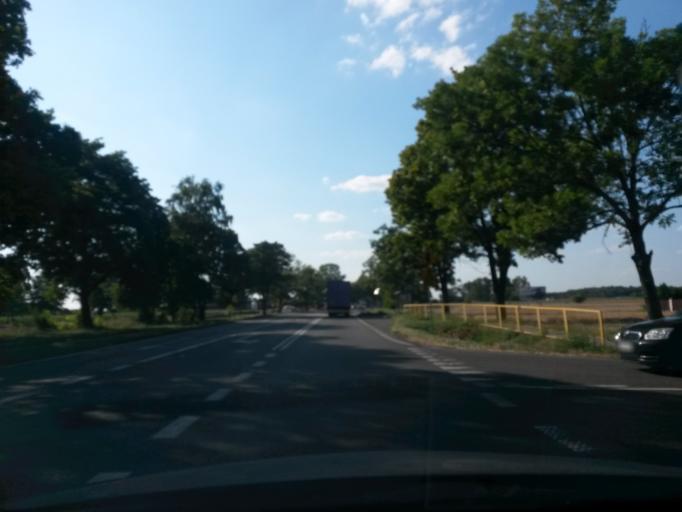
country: PL
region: Masovian Voivodeship
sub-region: Powiat sierpecki
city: Sierpc
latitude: 52.8448
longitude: 19.7164
